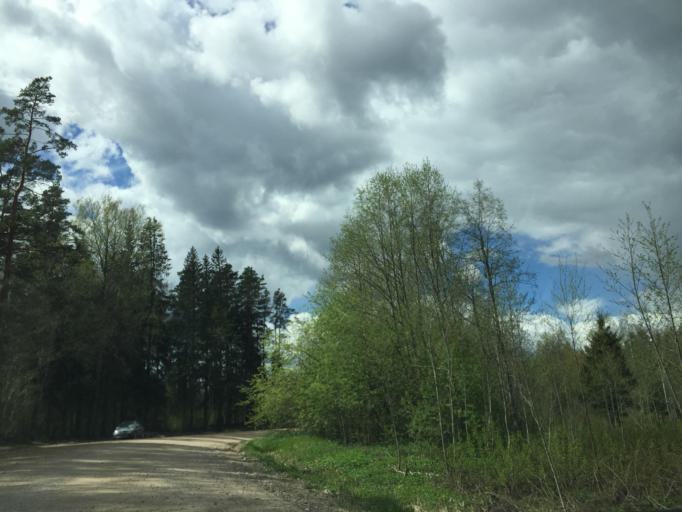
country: LV
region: Madonas Rajons
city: Madona
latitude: 56.9244
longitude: 26.0248
